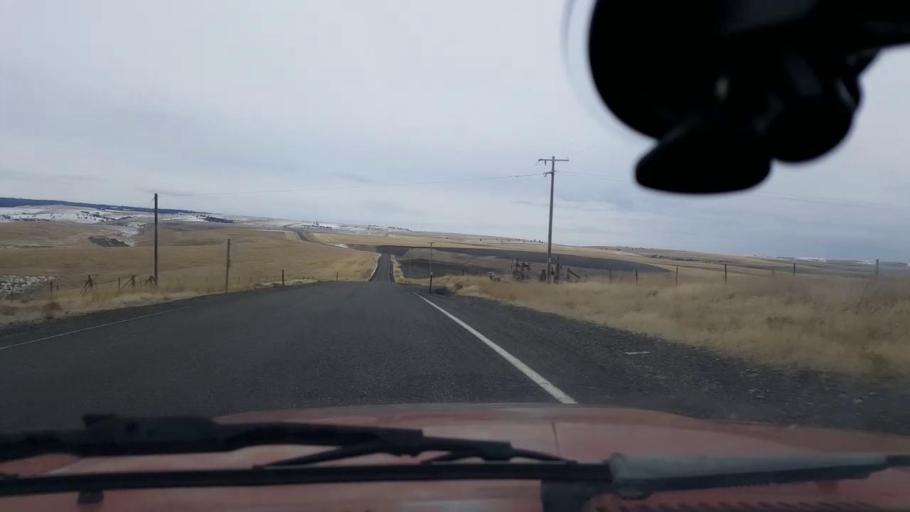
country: US
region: Washington
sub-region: Asotin County
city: Clarkston Heights-Vineland
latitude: 46.3239
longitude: -117.3552
